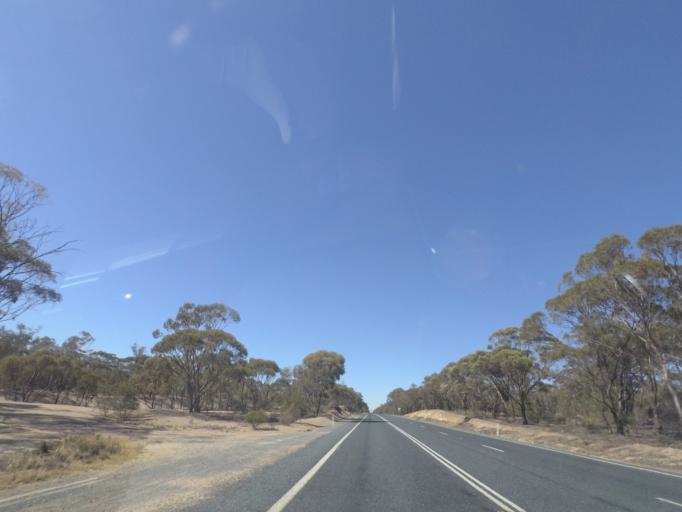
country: AU
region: New South Wales
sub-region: Bland
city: West Wyalong
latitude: -34.1274
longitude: 147.1249
